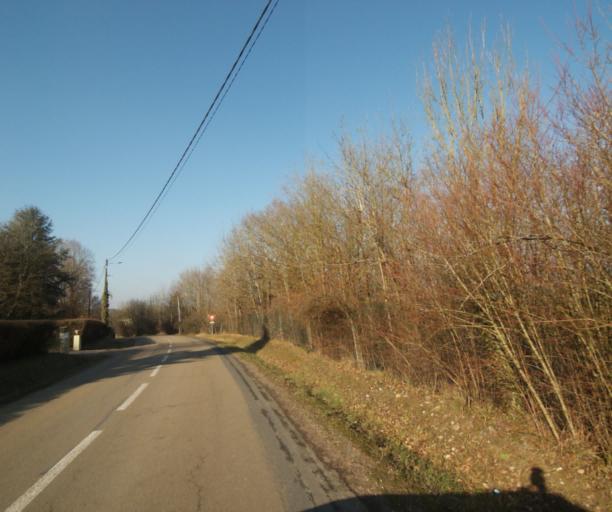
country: FR
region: Champagne-Ardenne
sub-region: Departement de la Haute-Marne
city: Wassy
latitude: 48.4954
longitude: 4.9378
